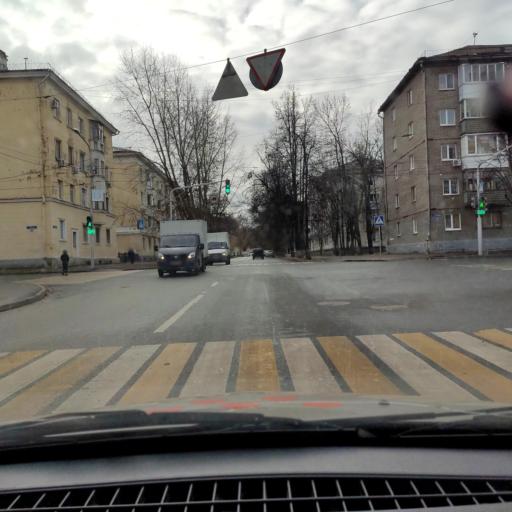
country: RU
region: Bashkortostan
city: Ufa
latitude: 54.8231
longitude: 56.0709
